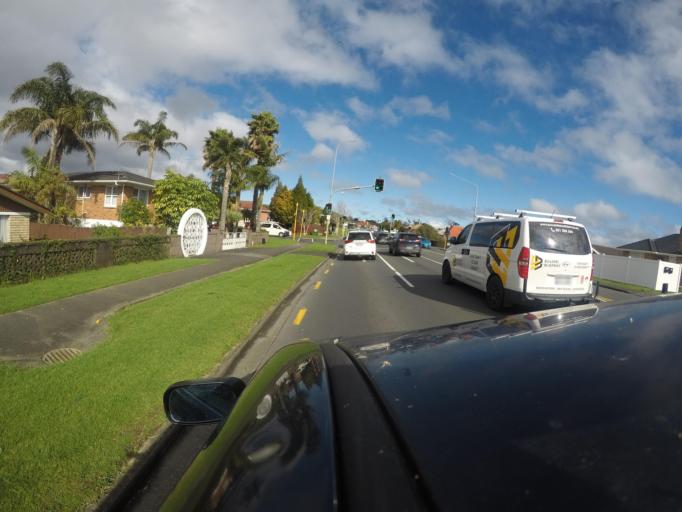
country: NZ
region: Auckland
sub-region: Auckland
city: Waitakere
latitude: -36.8934
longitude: 174.6450
